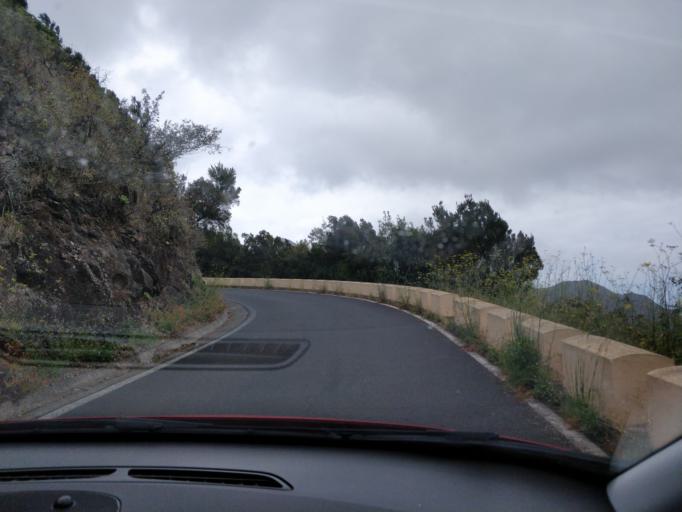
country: ES
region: Canary Islands
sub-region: Provincia de Santa Cruz de Tenerife
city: Santiago del Teide
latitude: 28.3222
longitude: -16.8485
